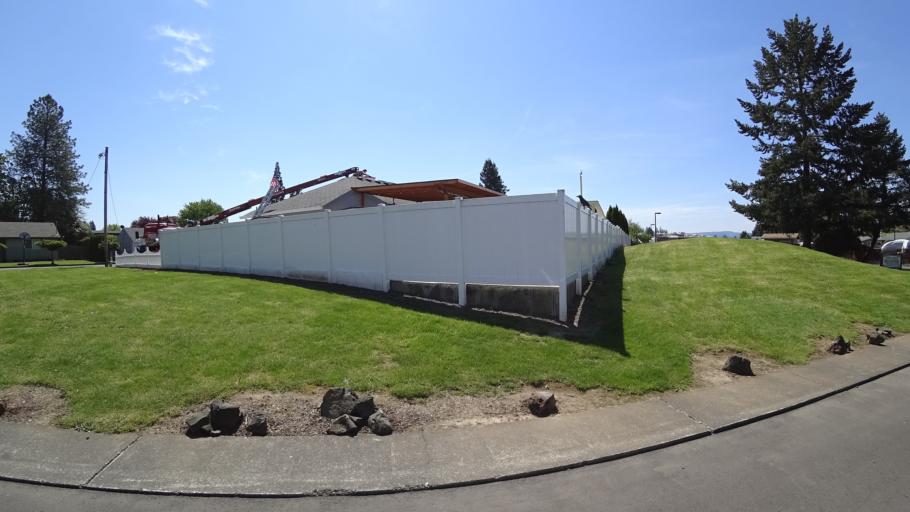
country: US
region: Oregon
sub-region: Washington County
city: Hillsboro
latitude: 45.5066
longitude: -122.9667
